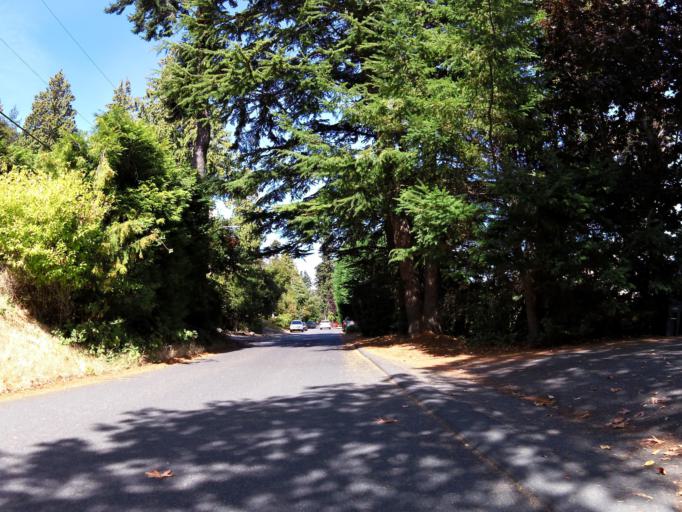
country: CA
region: British Columbia
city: Victoria
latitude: 48.5139
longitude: -123.3670
